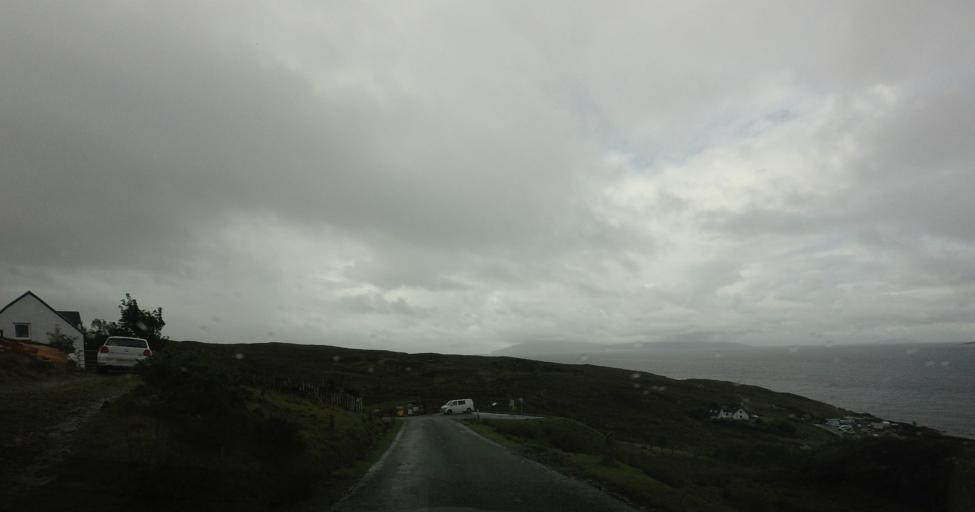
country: GB
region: Scotland
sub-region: Highland
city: Isle of Skye
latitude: 57.1464
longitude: -6.1029
